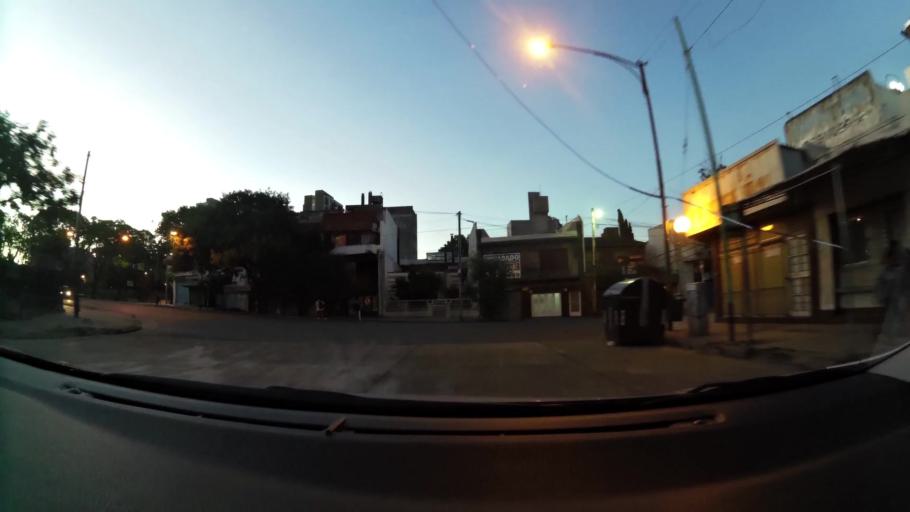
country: AR
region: Buenos Aires F.D.
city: Villa Lugano
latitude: -34.6457
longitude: -58.4510
